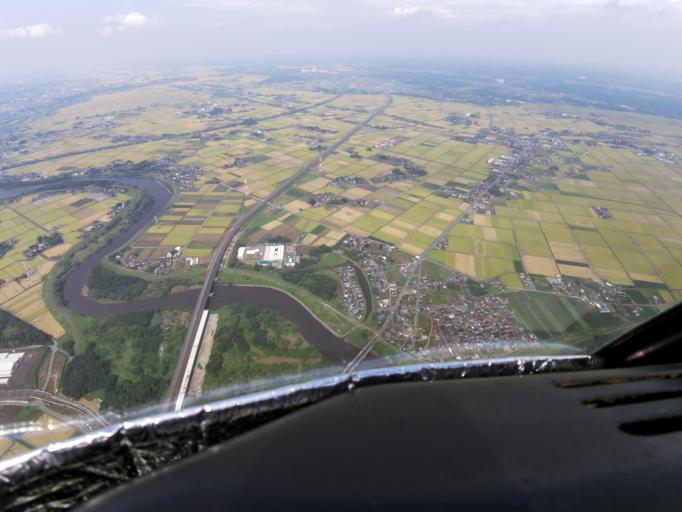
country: JP
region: Ibaraki
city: Moriya
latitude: 35.9555
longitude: 140.0059
